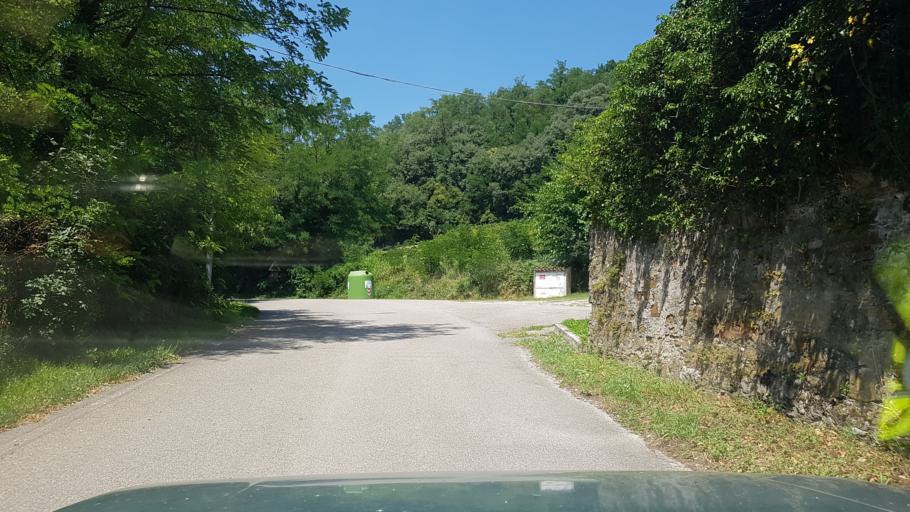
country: IT
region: Friuli Venezia Giulia
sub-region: Provincia di Gorizia
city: Farra d'Isonzo
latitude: 45.9057
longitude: 13.5409
